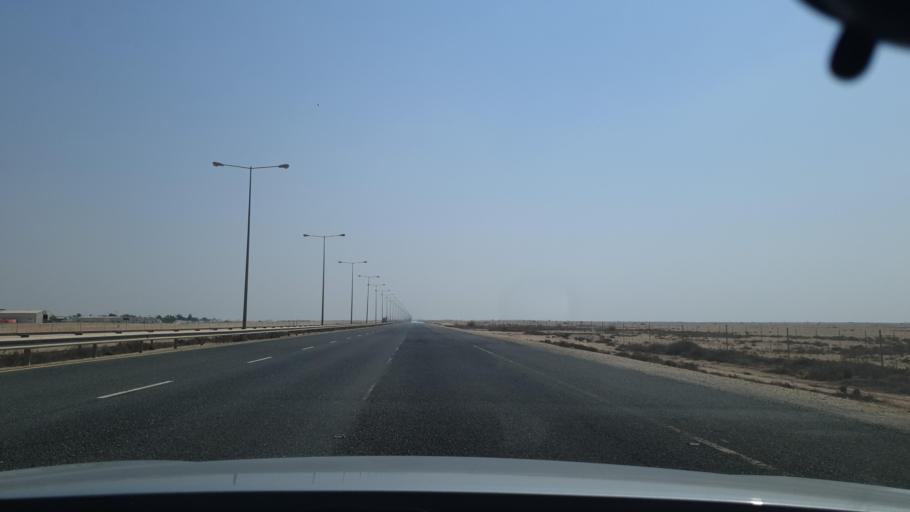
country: QA
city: Al Ghuwayriyah
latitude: 25.8165
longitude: 51.3692
